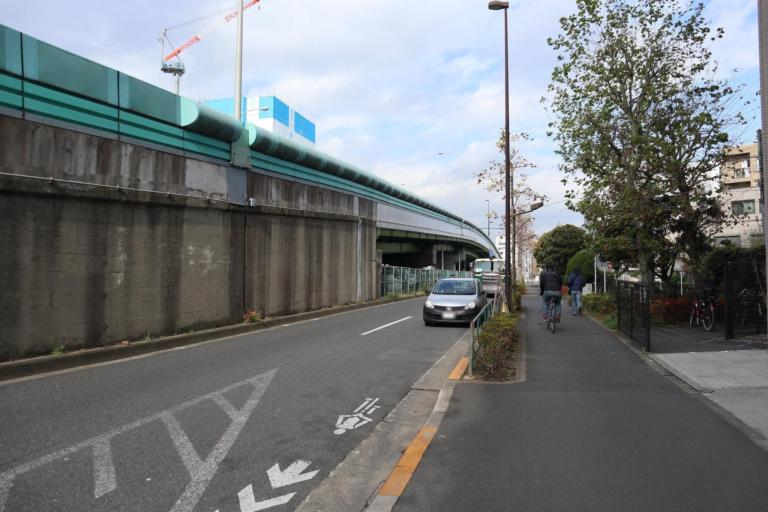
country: JP
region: Tokyo
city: Urayasu
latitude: 35.6865
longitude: 139.8826
